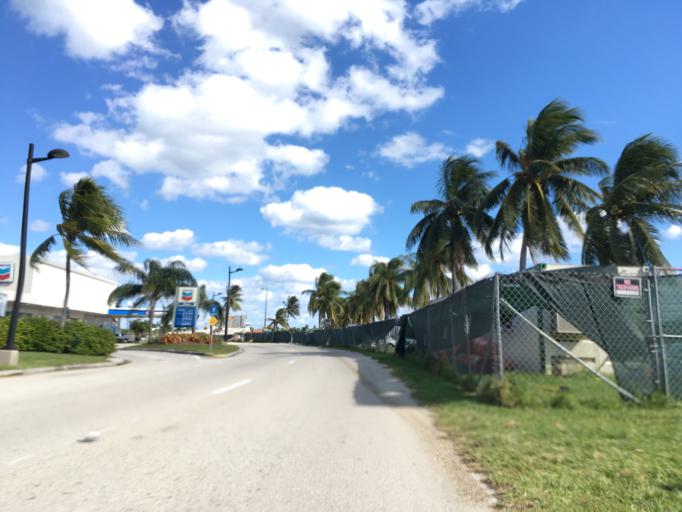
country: US
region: Florida
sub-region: Miami-Dade County
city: Bay Harbor Islands
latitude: 25.8878
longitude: -80.1457
